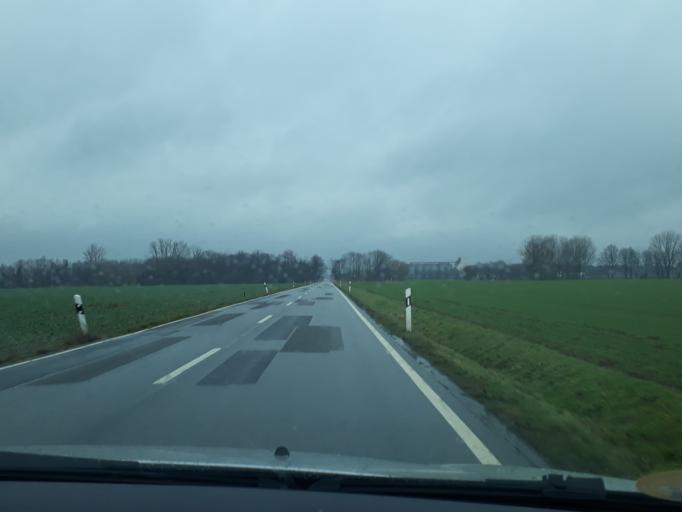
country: DE
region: Saxony
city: Malschwitz
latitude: 51.2412
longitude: 14.5300
